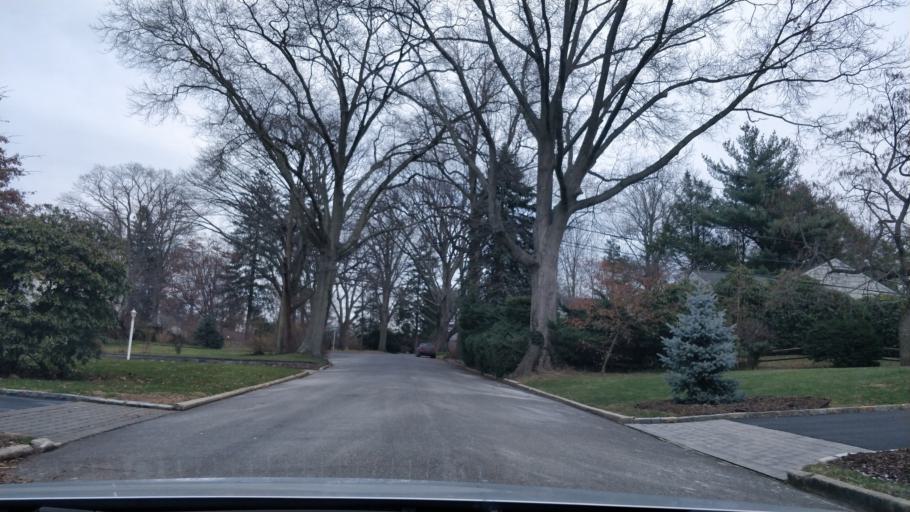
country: US
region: New York
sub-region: Nassau County
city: Glen Cove
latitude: 40.8664
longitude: -73.6494
